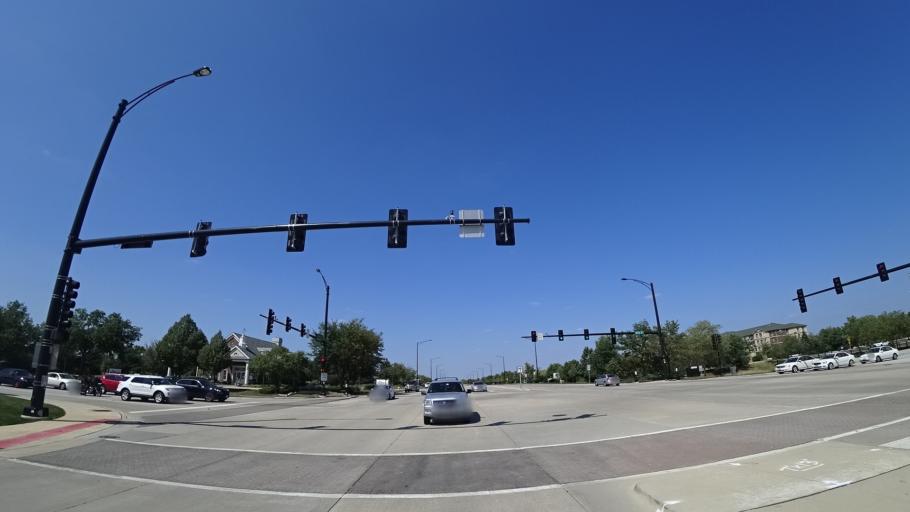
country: US
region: Illinois
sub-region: Cook County
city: Orland Hills
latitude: 41.5934
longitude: -87.8526
